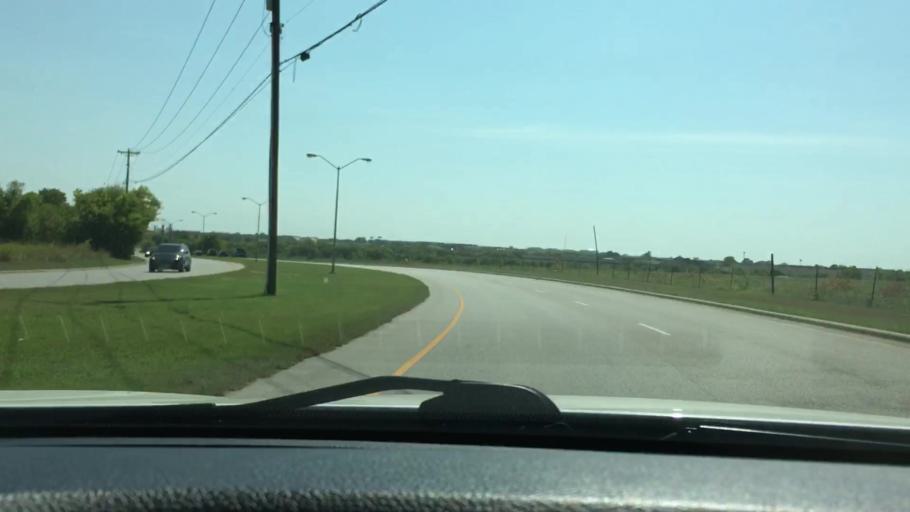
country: US
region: Texas
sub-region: Travis County
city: Windemere
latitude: 30.4795
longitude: -97.6637
